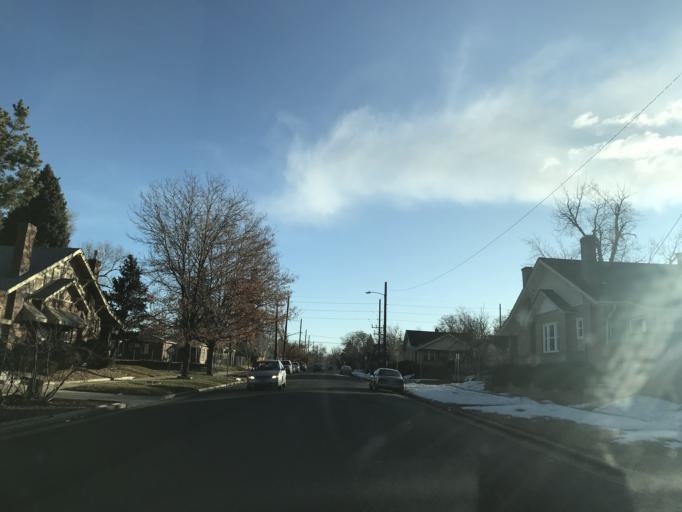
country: US
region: Colorado
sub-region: Denver County
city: Denver
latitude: 39.7658
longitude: -104.9630
